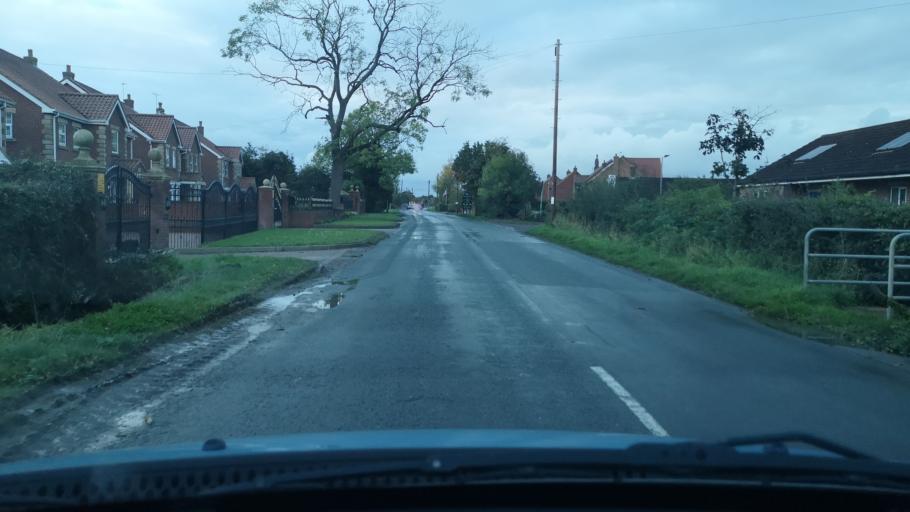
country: GB
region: England
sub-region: Doncaster
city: Moss
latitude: 53.6219
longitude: -1.0984
